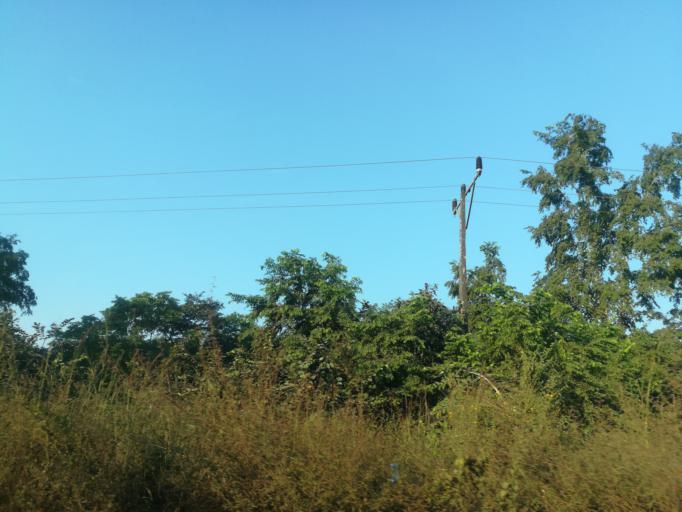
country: NG
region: Ogun
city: Abeokuta
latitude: 7.2128
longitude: 3.1956
